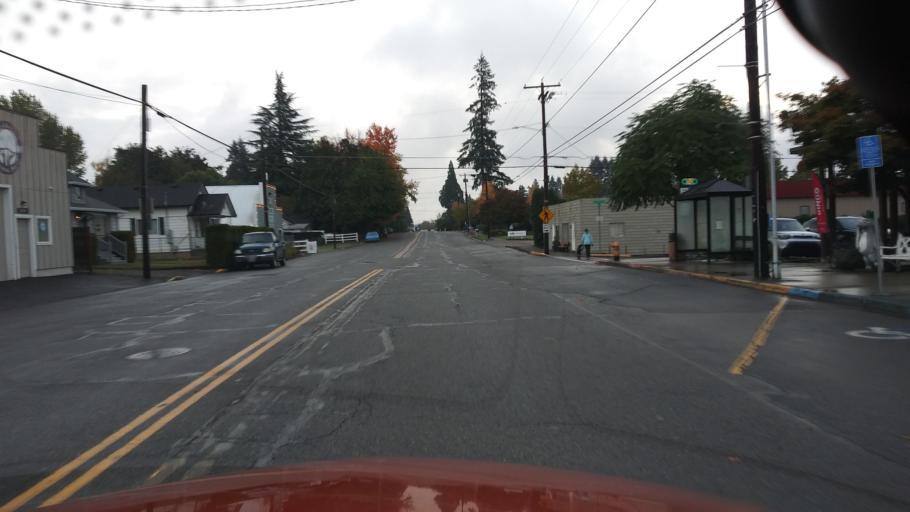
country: US
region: Oregon
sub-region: Washington County
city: North Plains
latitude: 45.5978
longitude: -123.0014
